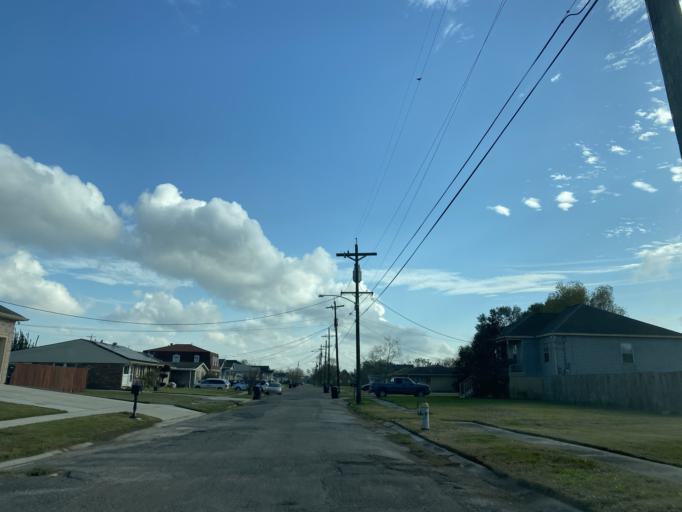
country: US
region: Louisiana
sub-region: Saint Bernard Parish
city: Arabi
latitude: 30.0288
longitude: -90.0377
